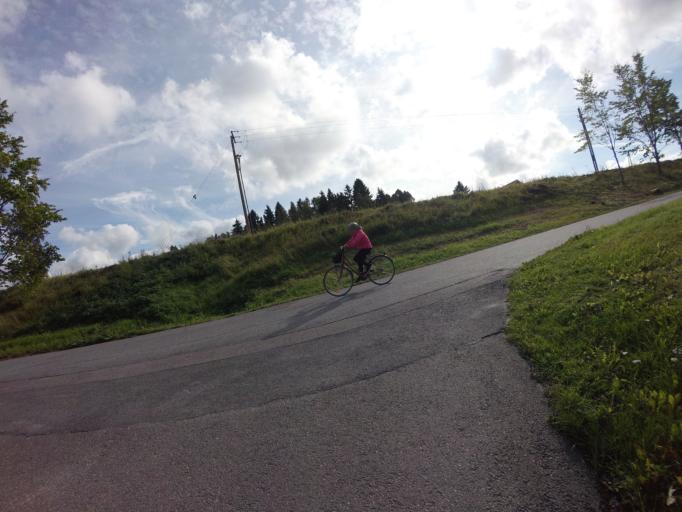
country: FI
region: Varsinais-Suomi
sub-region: Turku
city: Kaarina
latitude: 60.4642
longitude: 22.3359
